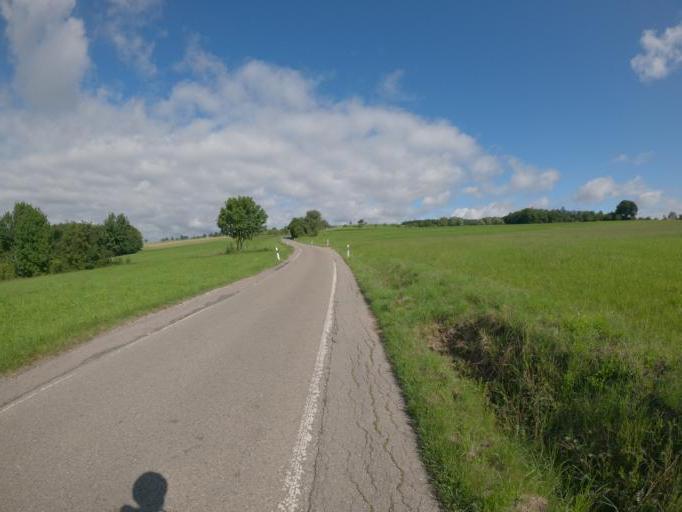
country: DE
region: Baden-Wuerttemberg
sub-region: Regierungsbezirk Stuttgart
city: Ebersbach an der Fils
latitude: 48.7278
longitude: 9.5422
